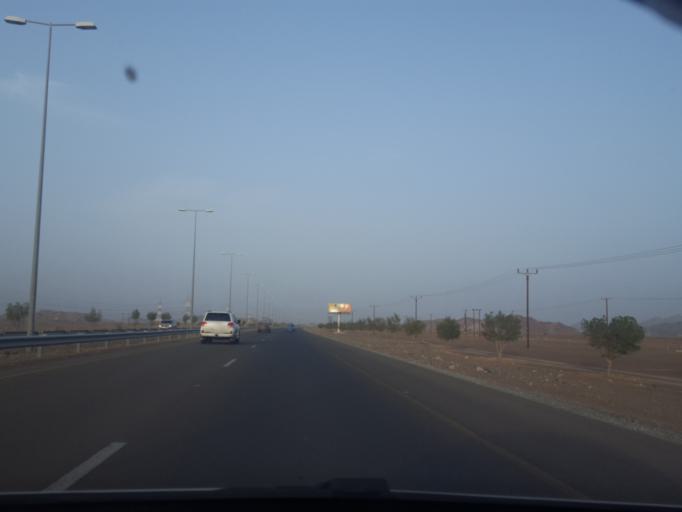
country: OM
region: Al Buraimi
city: Al Buraymi
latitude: 24.2450
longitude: 55.9933
